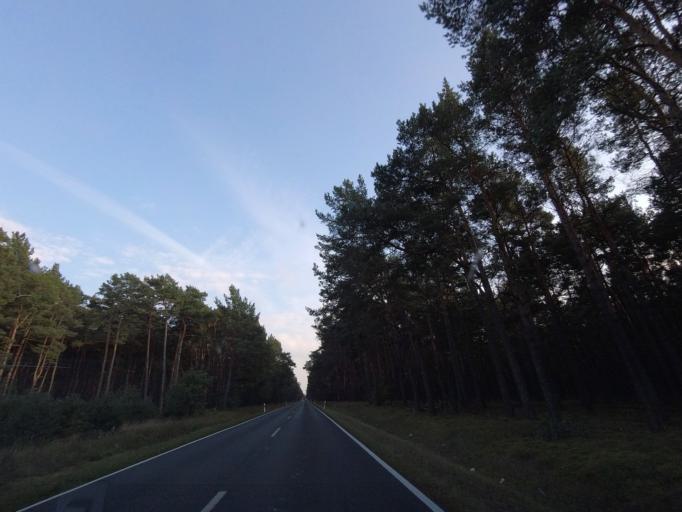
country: DE
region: Brandenburg
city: Bruck
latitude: 52.1740
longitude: 12.7610
